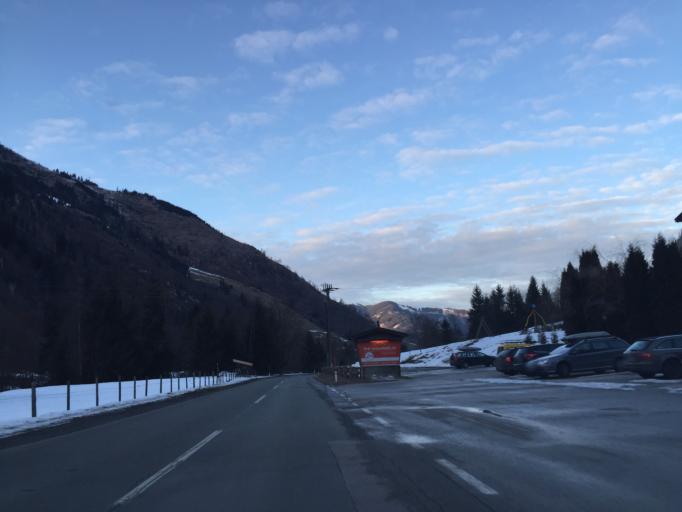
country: AT
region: Salzburg
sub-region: Politischer Bezirk Zell am See
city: Kaprun
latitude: 47.2382
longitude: 12.7310
